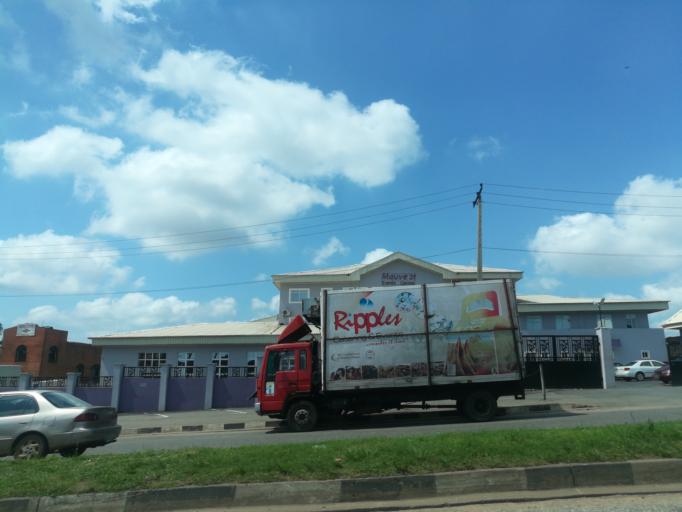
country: NG
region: Oyo
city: Ibadan
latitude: 7.3595
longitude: 3.8711
